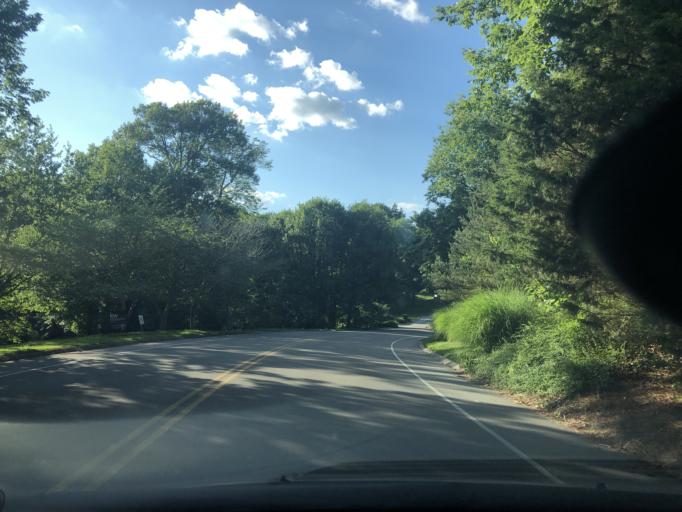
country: US
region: Tennessee
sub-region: Davidson County
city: Forest Hills
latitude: 36.0576
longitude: -86.8318
